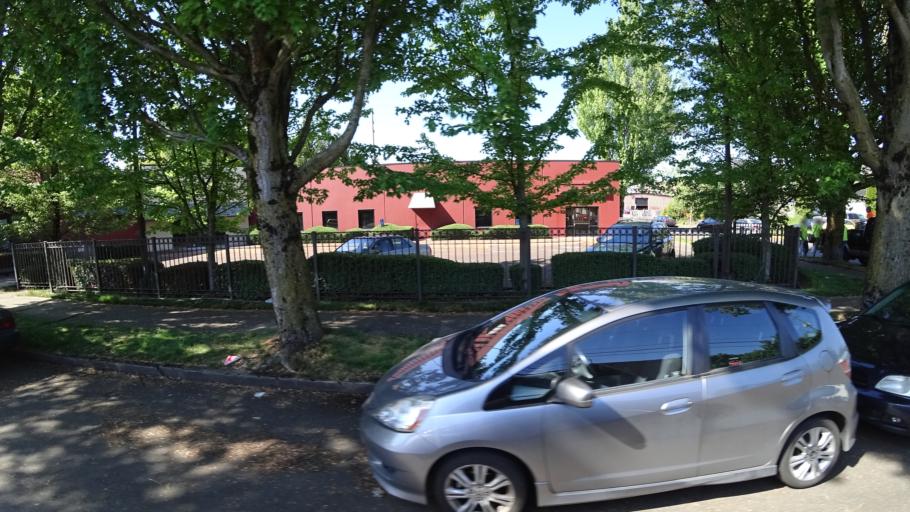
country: US
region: Oregon
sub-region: Multnomah County
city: Portland
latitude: 45.5358
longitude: -122.6628
